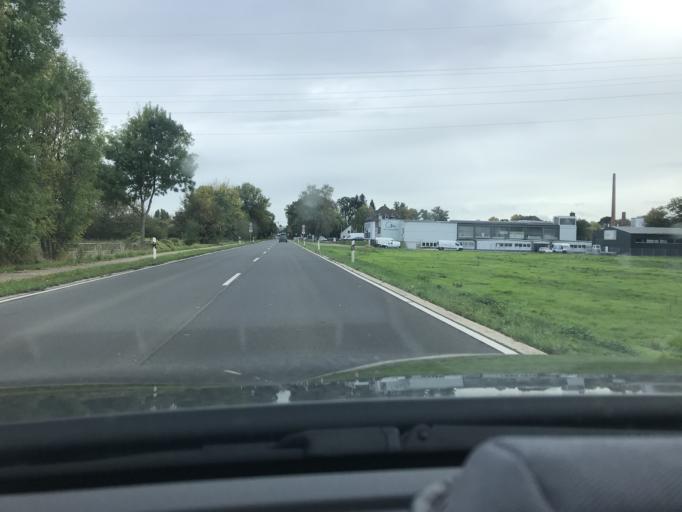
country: DE
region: North Rhine-Westphalia
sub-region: Regierungsbezirk Koln
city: Dueren
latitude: 50.8061
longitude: 6.4598
